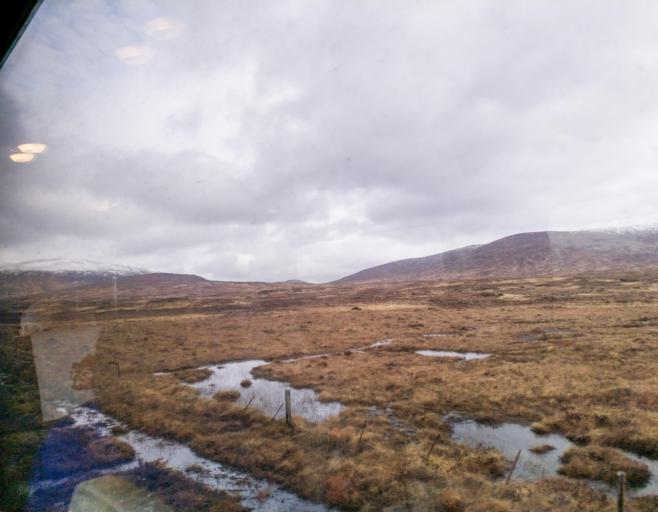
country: GB
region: Scotland
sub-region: Highland
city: Spean Bridge
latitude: 56.7338
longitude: -4.6532
